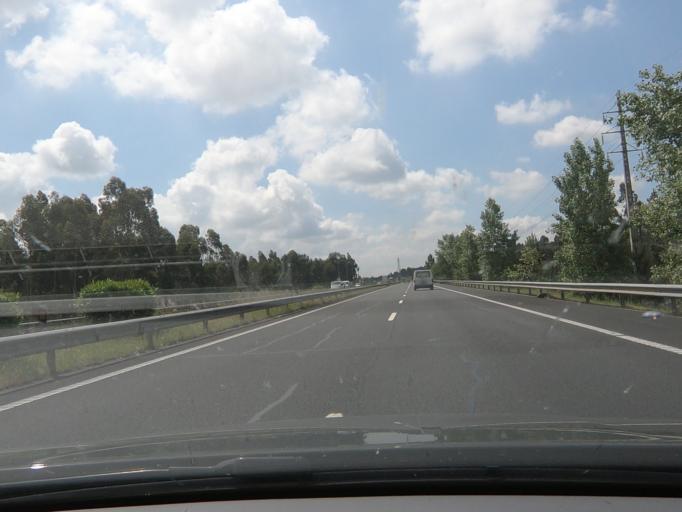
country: PT
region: Leiria
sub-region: Caldas da Rainha
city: Caldas da Rainha
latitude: 39.3929
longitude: -9.1526
